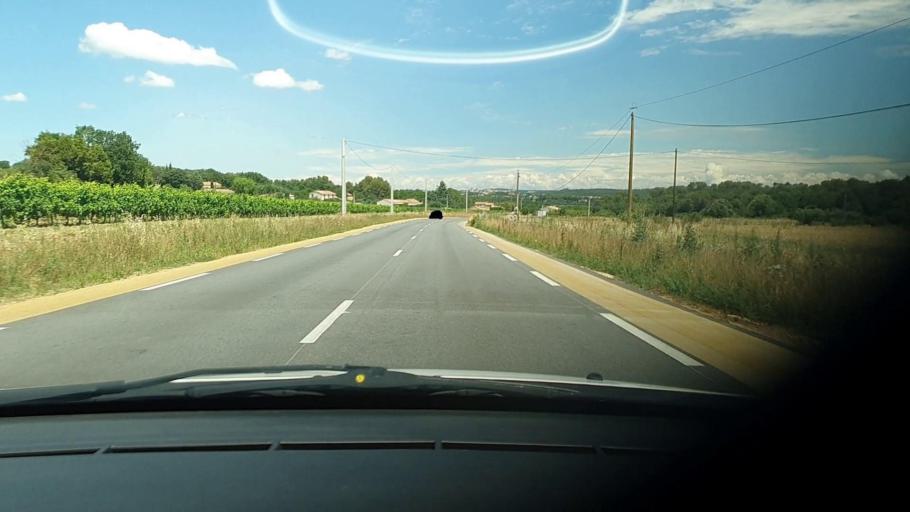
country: FR
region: Languedoc-Roussillon
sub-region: Departement du Gard
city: Blauzac
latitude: 43.9863
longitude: 4.3771
